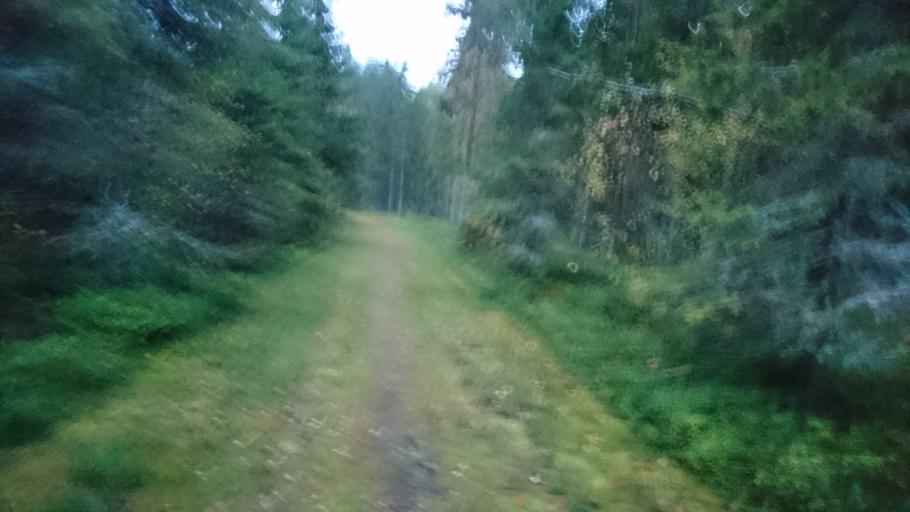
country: SE
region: Vaesterbotten
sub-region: Robertsfors Kommun
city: Robertsfors
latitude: 64.2306
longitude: 20.9955
